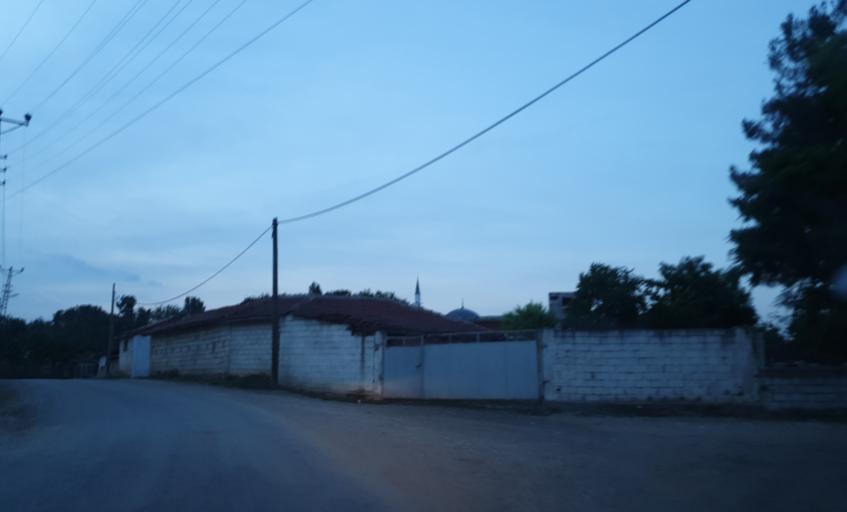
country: TR
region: Kirklareli
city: Vize
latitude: 41.4864
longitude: 27.7530
